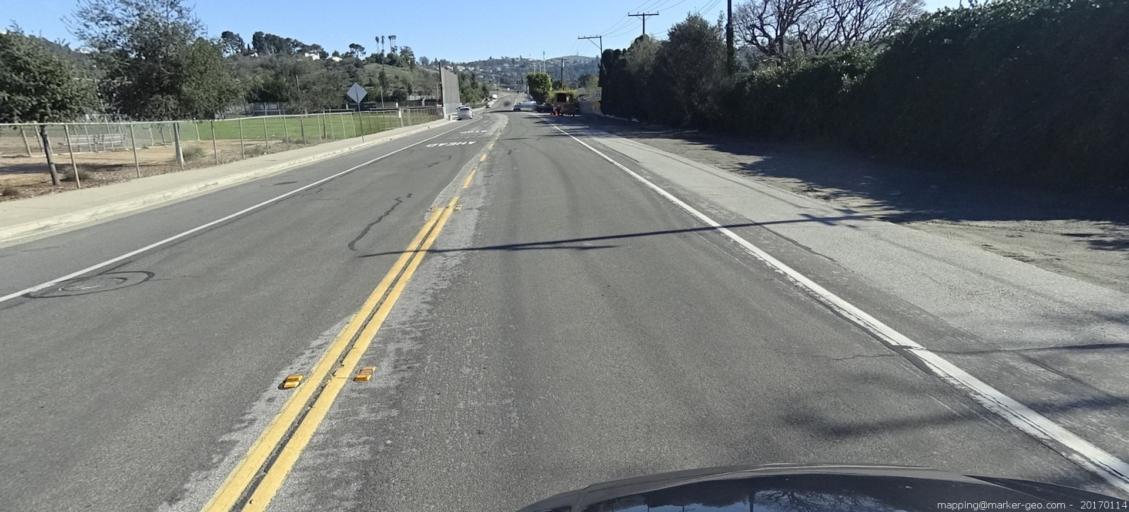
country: US
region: California
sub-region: Orange County
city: North Tustin
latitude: 33.7689
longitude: -117.8048
